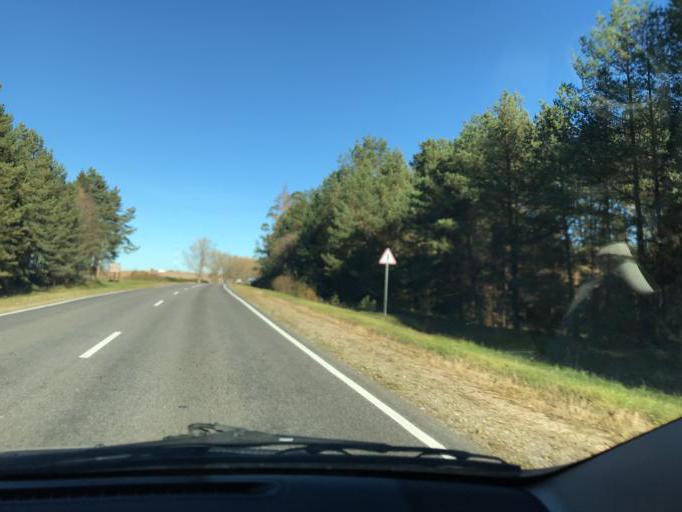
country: BY
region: Vitebsk
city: Lyepyel'
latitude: 54.9947
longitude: 28.7378
